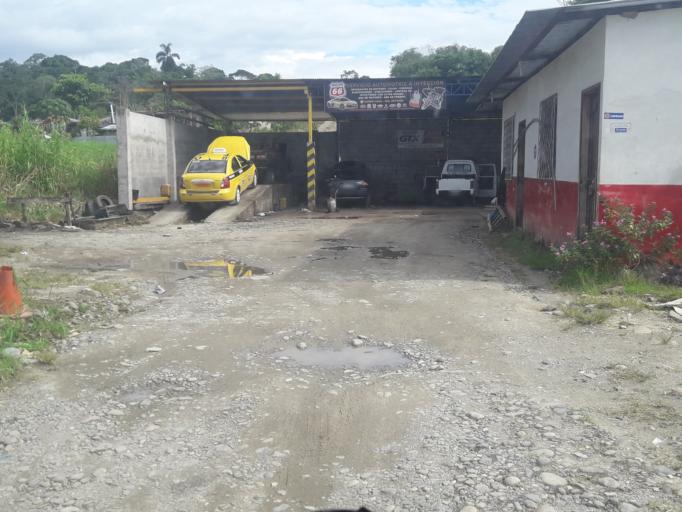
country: EC
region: Napo
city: Tena
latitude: -1.0071
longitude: -77.8175
